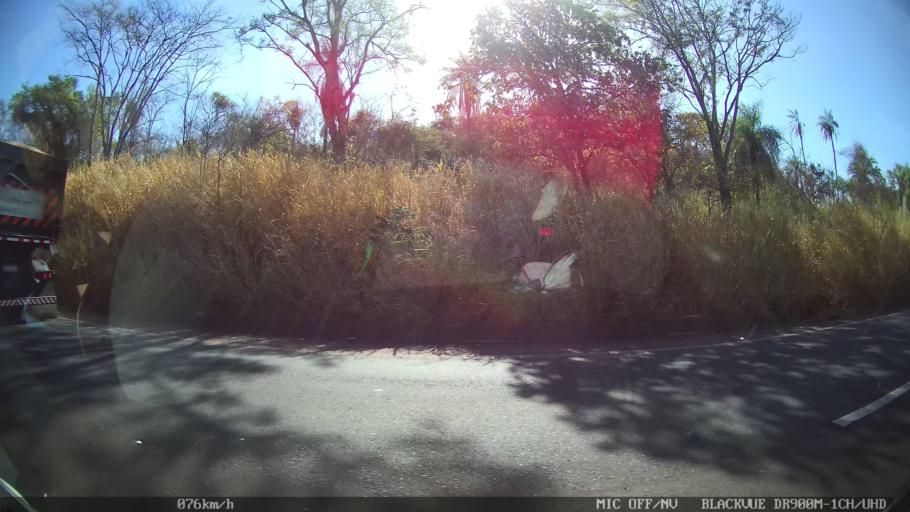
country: BR
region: Sao Paulo
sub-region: Barretos
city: Barretos
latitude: -20.5957
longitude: -48.7174
